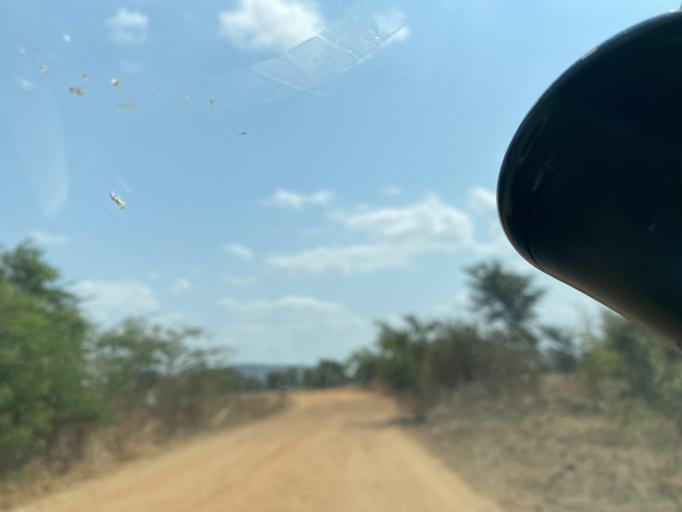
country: ZM
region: Lusaka
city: Chongwe
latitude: -15.5880
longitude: 28.7619
